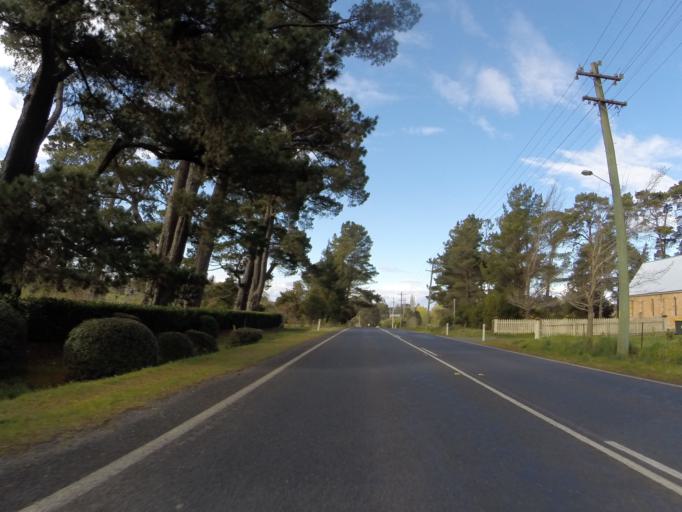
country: AU
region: New South Wales
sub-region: Wingecarribee
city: Moss Vale
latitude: -34.5743
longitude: 150.3125
